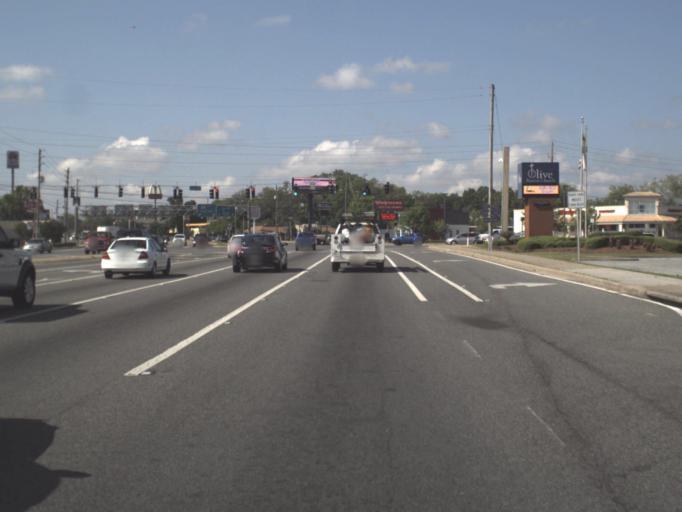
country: US
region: Florida
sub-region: Escambia County
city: Ferry Pass
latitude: 30.5112
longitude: -87.2202
